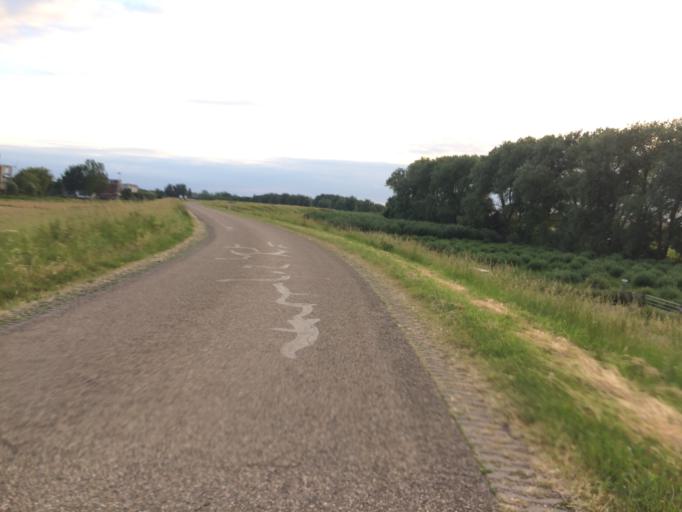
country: NL
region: North Brabant
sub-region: Gemeente 's-Hertogenbosch
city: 's-Hertogenbosch
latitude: 51.7389
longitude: 5.3259
